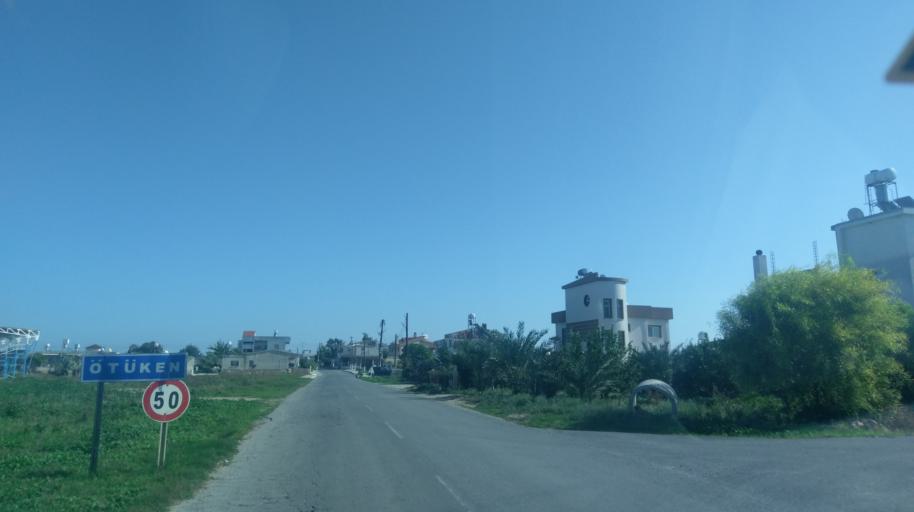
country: CY
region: Ammochostos
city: Trikomo
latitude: 35.2361
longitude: 33.8692
